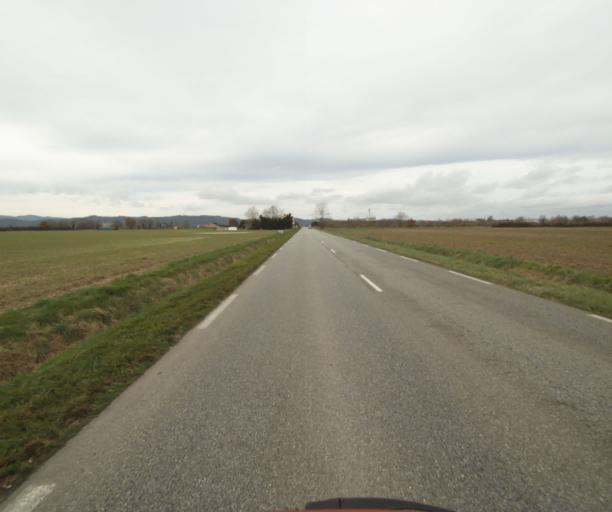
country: FR
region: Midi-Pyrenees
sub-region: Departement de l'Ariege
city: La Tour-du-Crieu
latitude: 43.0957
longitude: 1.6639
